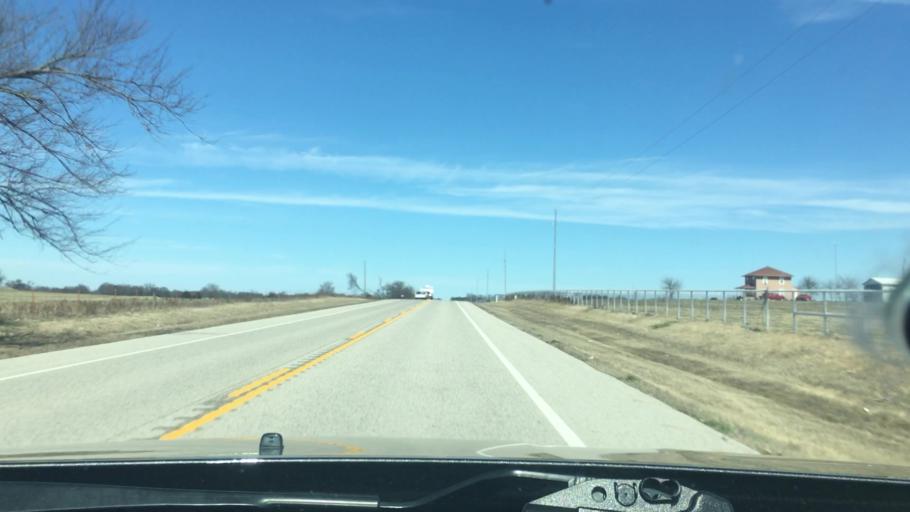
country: US
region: Oklahoma
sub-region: Murray County
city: Sulphur
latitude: 34.3778
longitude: -96.9508
